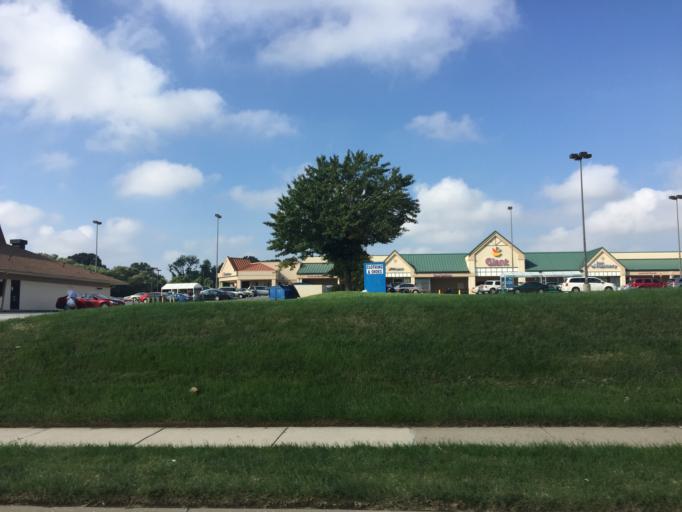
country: US
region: Maryland
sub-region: Baltimore County
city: Dundalk
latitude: 39.2778
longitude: -76.5045
